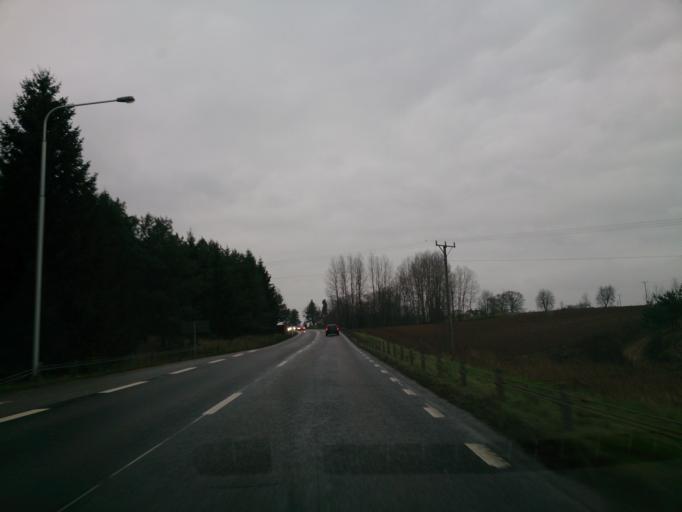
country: SE
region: OEstergoetland
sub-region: Linkopings Kommun
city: Sturefors
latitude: 58.3153
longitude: 15.8724
